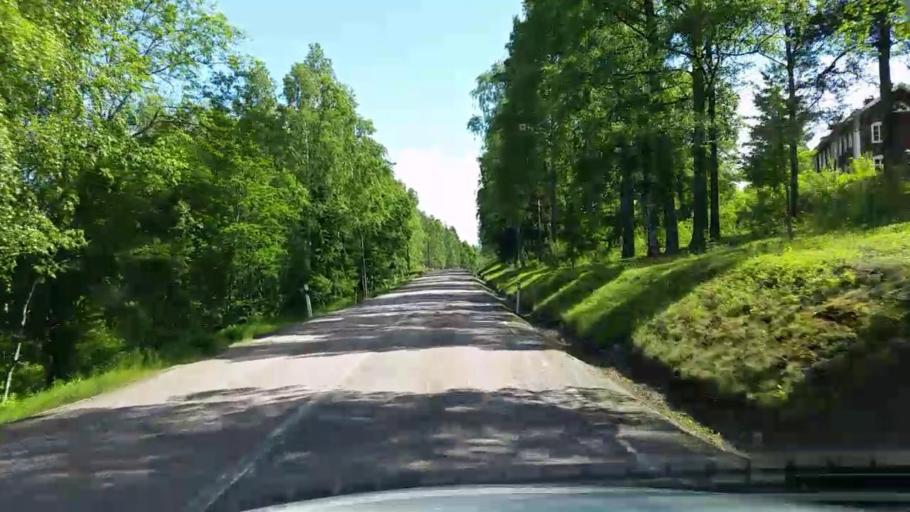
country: SE
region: Vaestmanland
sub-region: Kopings Kommun
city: Kolsva
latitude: 59.6814
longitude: 15.7640
